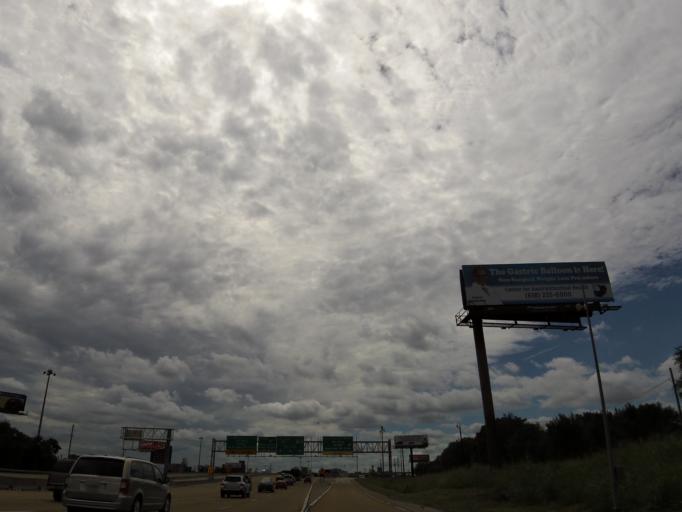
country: US
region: Illinois
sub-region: Saint Clair County
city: East Saint Louis
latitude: 38.6313
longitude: -90.1531
